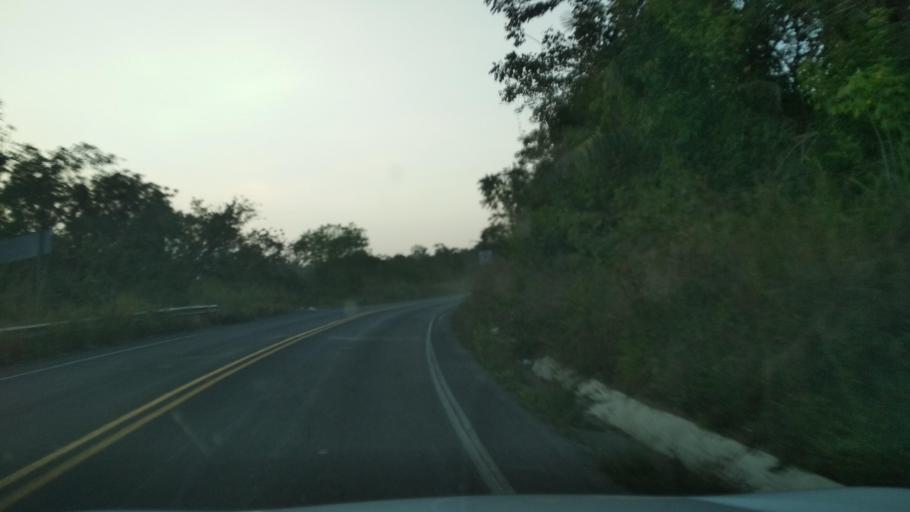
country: MX
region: Veracruz
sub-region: Poza Rica de Hidalgo
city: Arroyo del Maiz Uno
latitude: 20.4794
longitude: -97.3884
